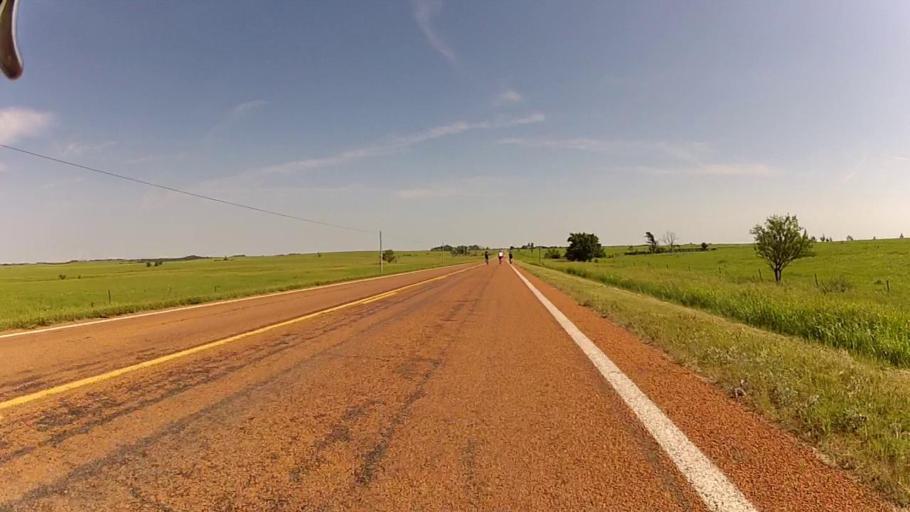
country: US
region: Kansas
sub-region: Cowley County
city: Winfield
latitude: 37.0736
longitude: -96.6436
